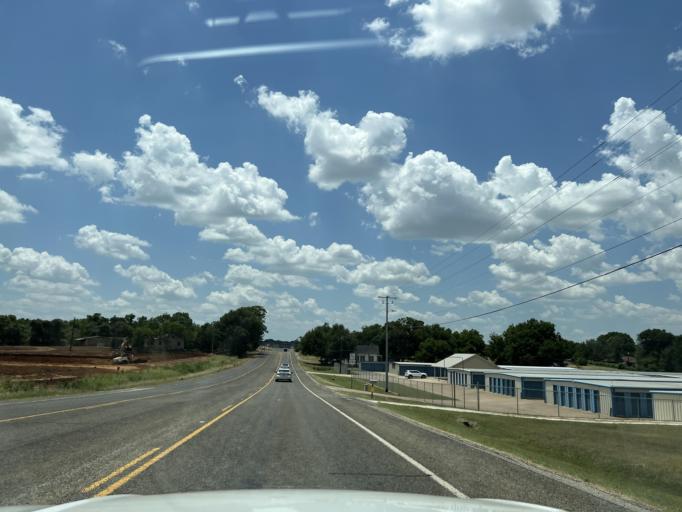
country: US
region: Texas
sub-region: Washington County
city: Brenham
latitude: 30.1471
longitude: -96.3776
